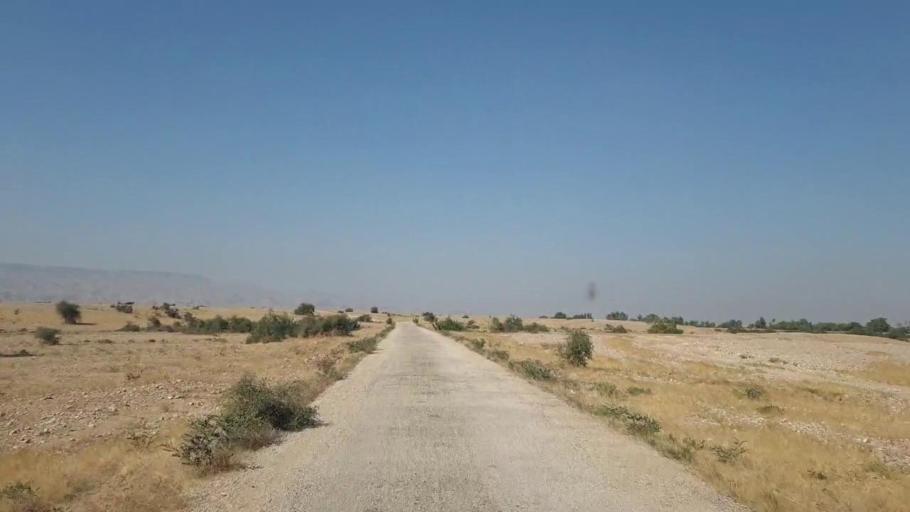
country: PK
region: Sindh
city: Jamshoro
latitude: 25.4798
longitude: 67.8378
